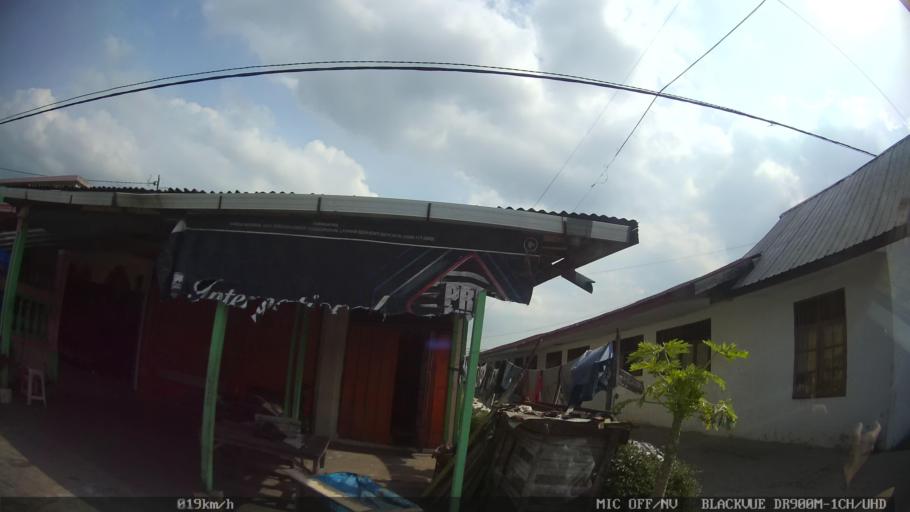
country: ID
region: North Sumatra
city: Binjai
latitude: 3.6064
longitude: 98.4993
